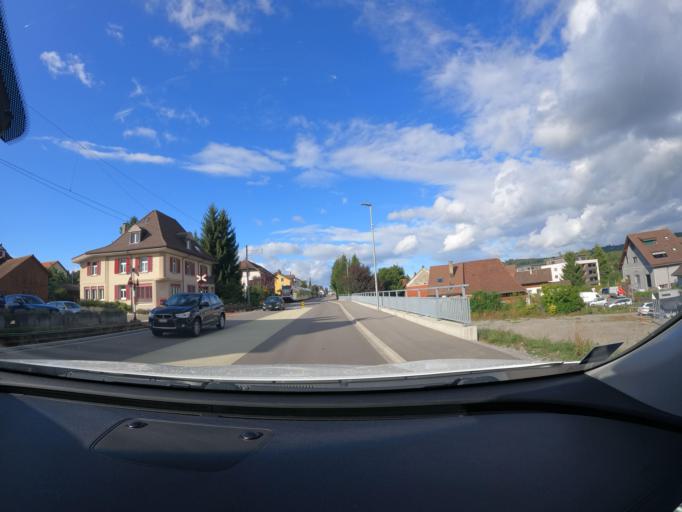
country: CH
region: Aargau
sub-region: Bezirk Lenzburg
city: Seon
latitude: 47.3491
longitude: 8.1590
